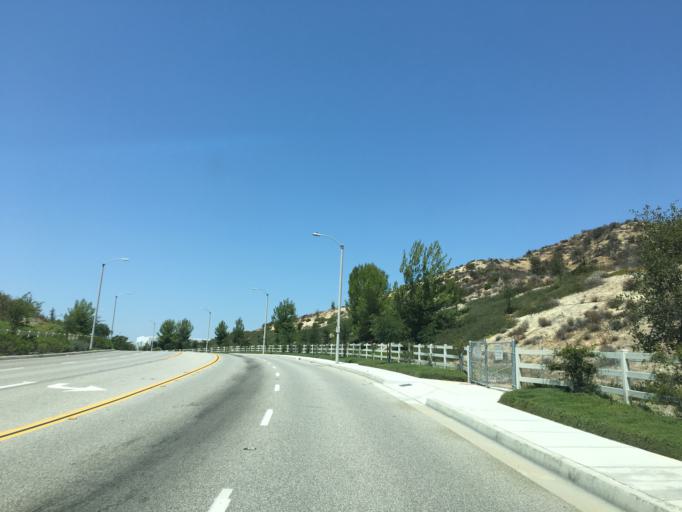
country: US
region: California
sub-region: Los Angeles County
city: Valencia
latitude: 34.4485
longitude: -118.5725
